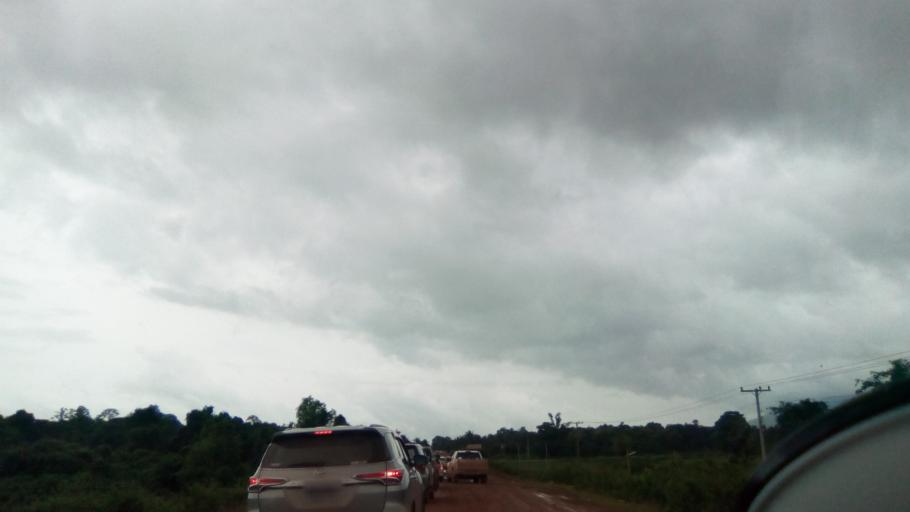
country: LA
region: Attapu
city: Attapu
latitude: 14.7511
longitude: 106.7020
